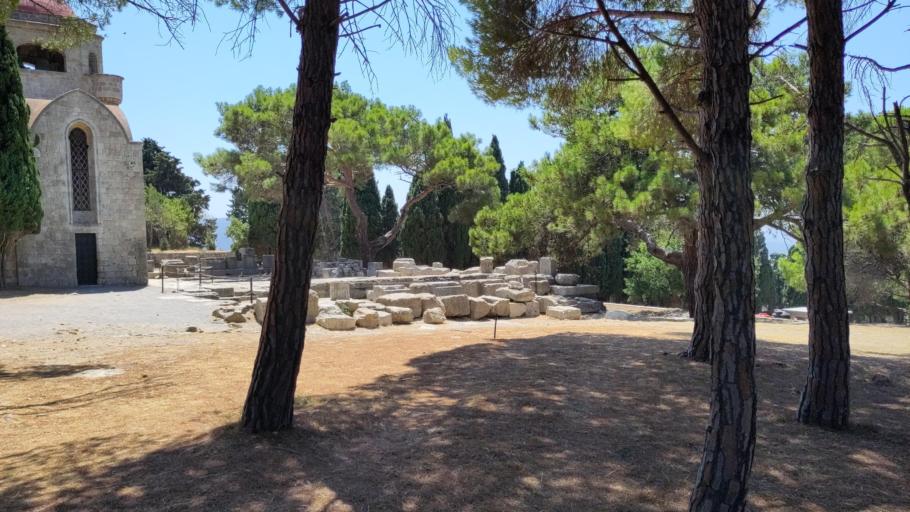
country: GR
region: South Aegean
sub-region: Nomos Dodekanisou
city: Trianta
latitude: 36.3993
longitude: 28.1443
